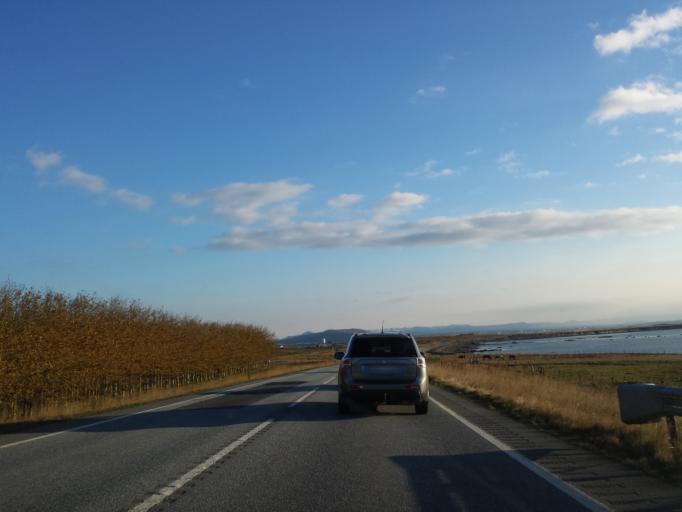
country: IS
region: Capital Region
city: Reykjavik
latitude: 64.2359
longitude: -21.8208
